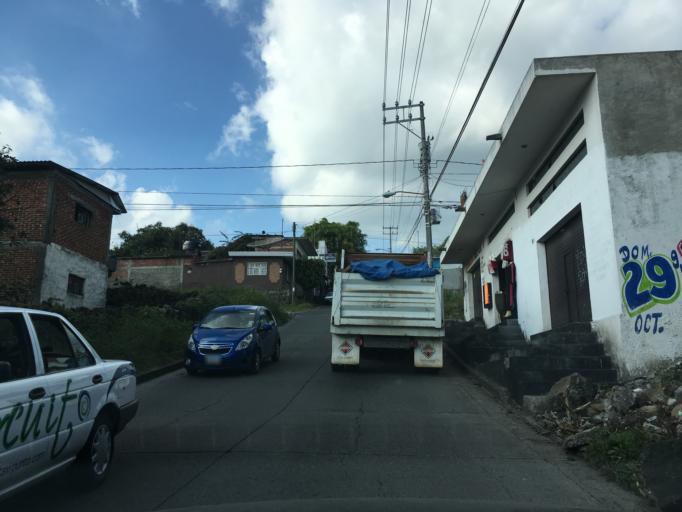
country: MX
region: Michoacan
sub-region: Uruapan
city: Uruapan
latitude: 19.4248
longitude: -102.0788
